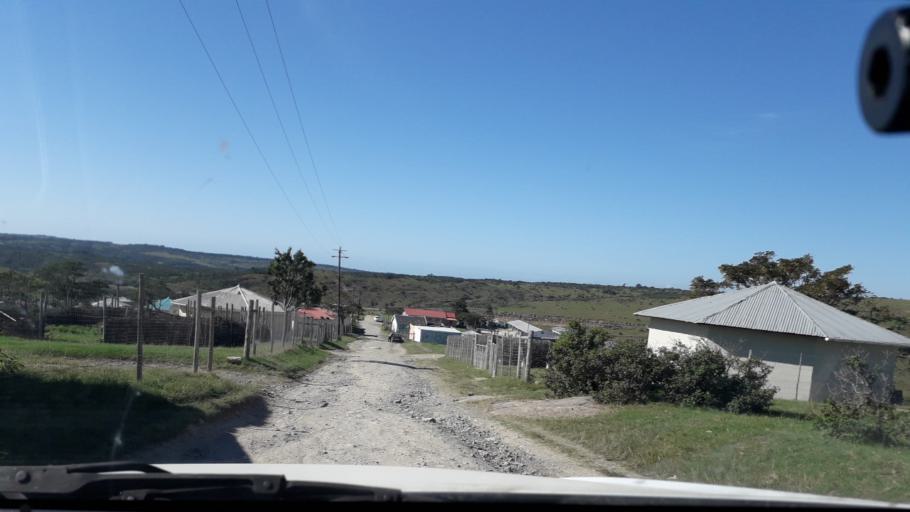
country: ZA
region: Eastern Cape
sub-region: Buffalo City Metropolitan Municipality
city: East London
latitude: -32.8458
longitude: 27.9899
